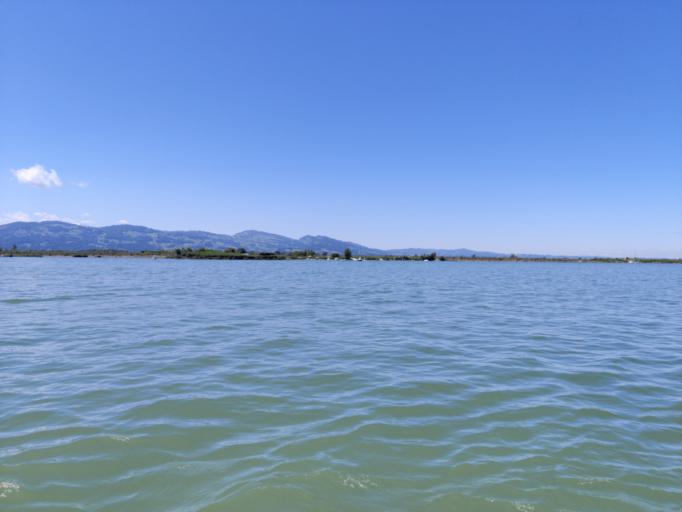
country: DE
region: Bavaria
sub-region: Swabia
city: Lindau
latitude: 47.5156
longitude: 9.6657
